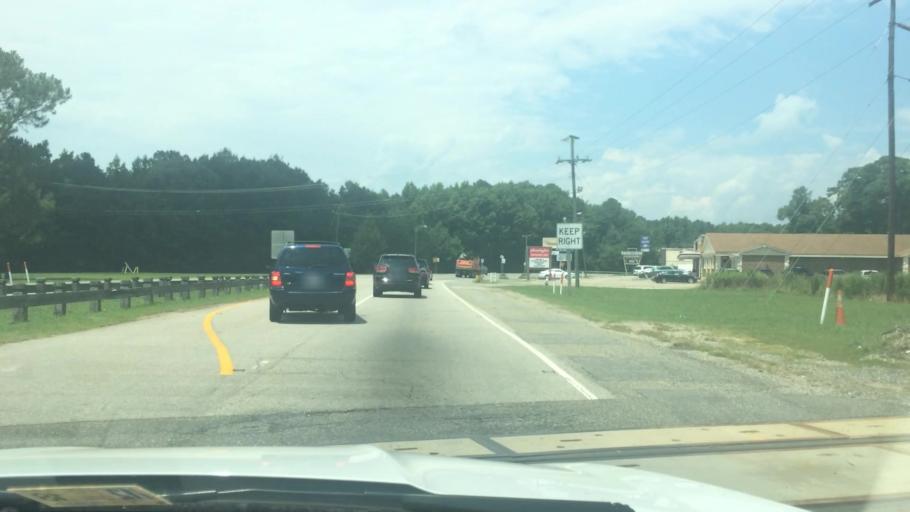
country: US
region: Virginia
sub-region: York County
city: Yorktown
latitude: 37.1749
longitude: -76.5688
